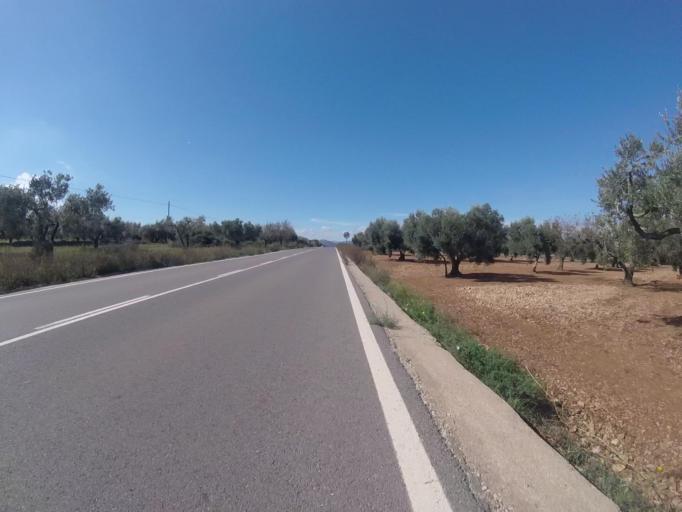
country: ES
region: Valencia
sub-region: Provincia de Castello
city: Albocasser
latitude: 40.3506
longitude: 0.0080
